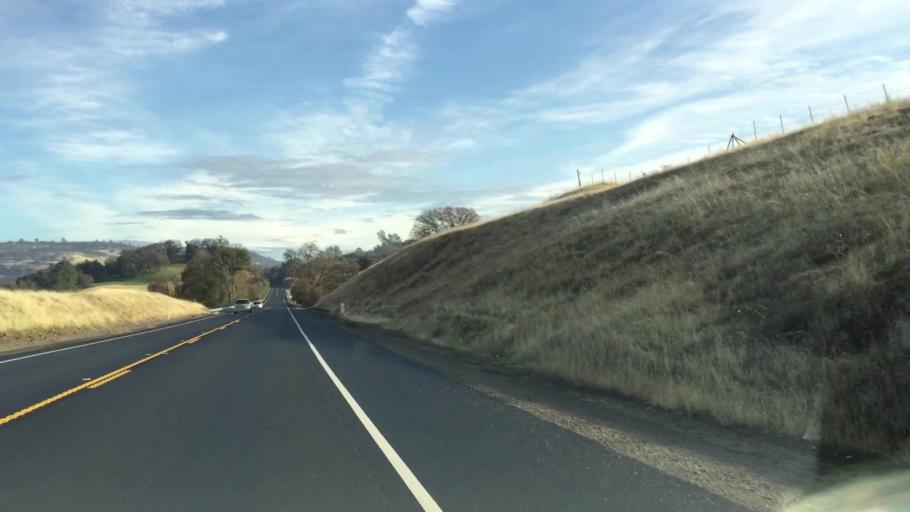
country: US
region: California
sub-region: Butte County
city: Oroville
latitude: 39.6359
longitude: -121.5808
